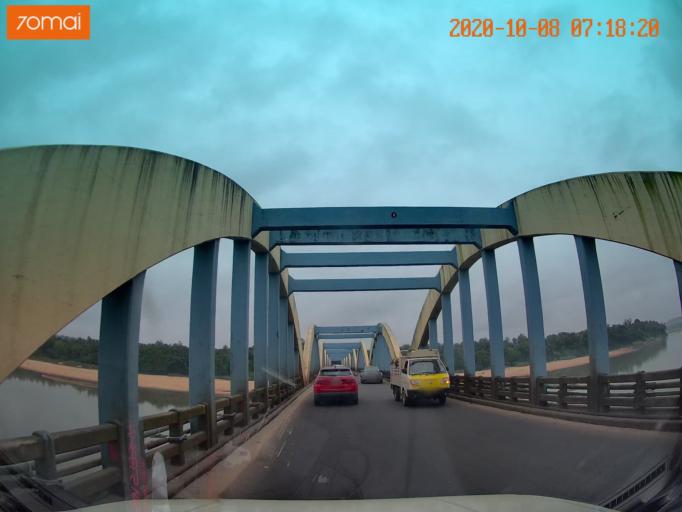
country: IN
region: Kerala
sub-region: Malappuram
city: Ponnani
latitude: 10.8405
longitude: 76.0225
